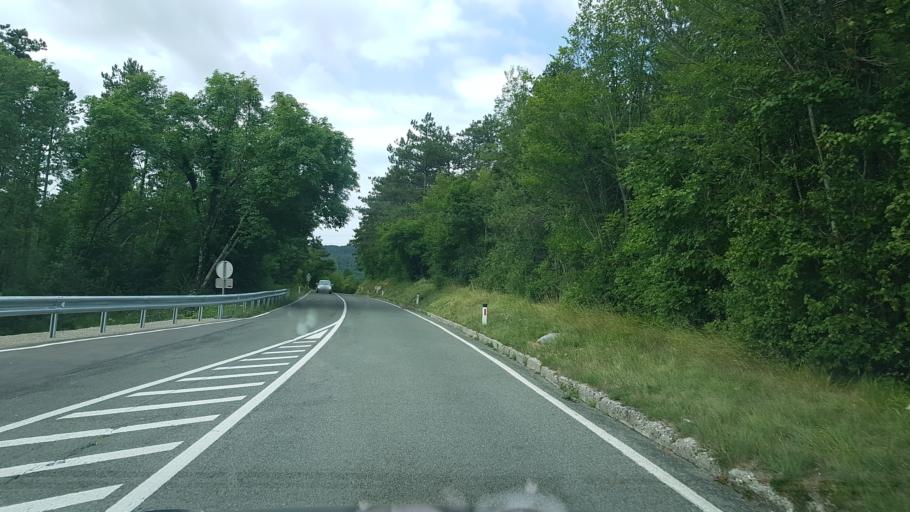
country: SI
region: Divaca
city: Divaca
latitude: 45.6642
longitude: 13.9408
